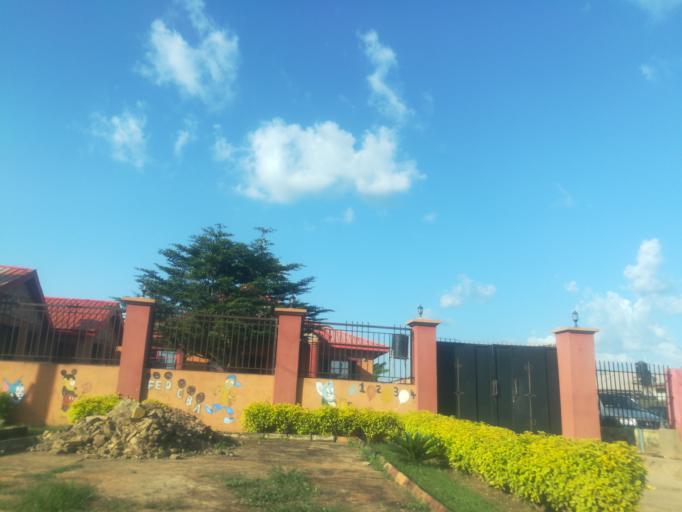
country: NG
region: Oyo
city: Ibadan
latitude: 7.4362
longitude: 3.9709
